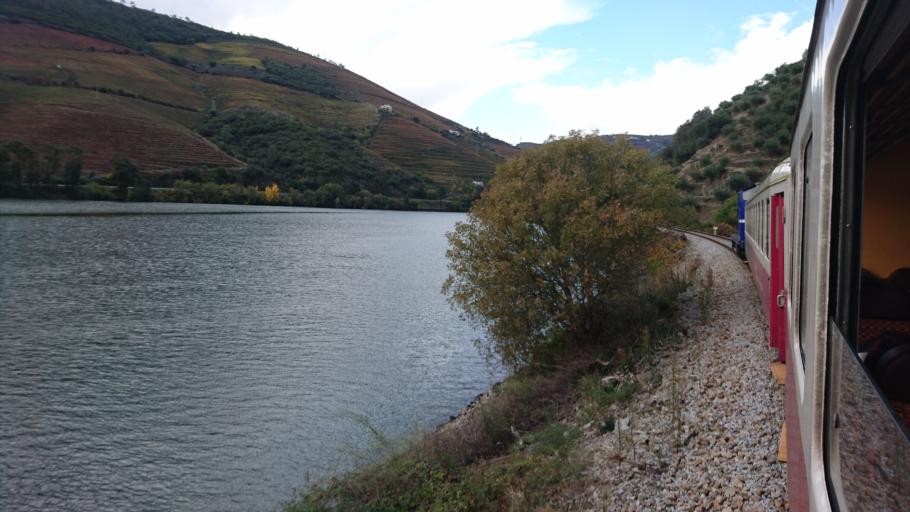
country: PT
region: Vila Real
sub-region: Sabrosa
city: Vilela
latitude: 41.1615
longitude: -7.6243
